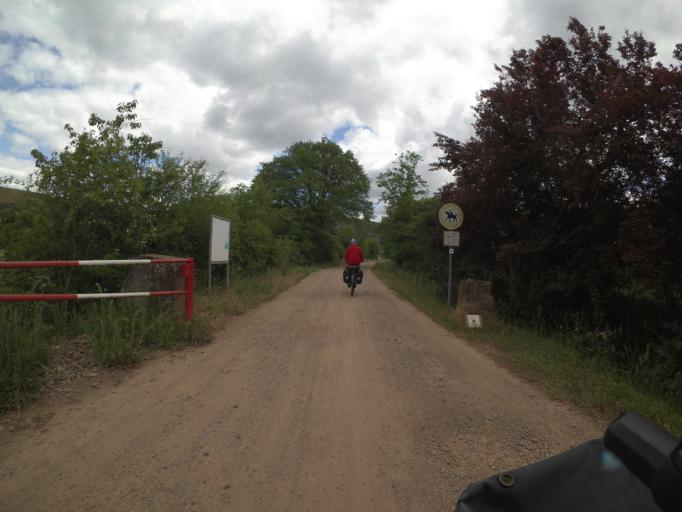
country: DE
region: Rheinland-Pfalz
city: Niederhausen
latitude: 49.8096
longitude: 7.7900
